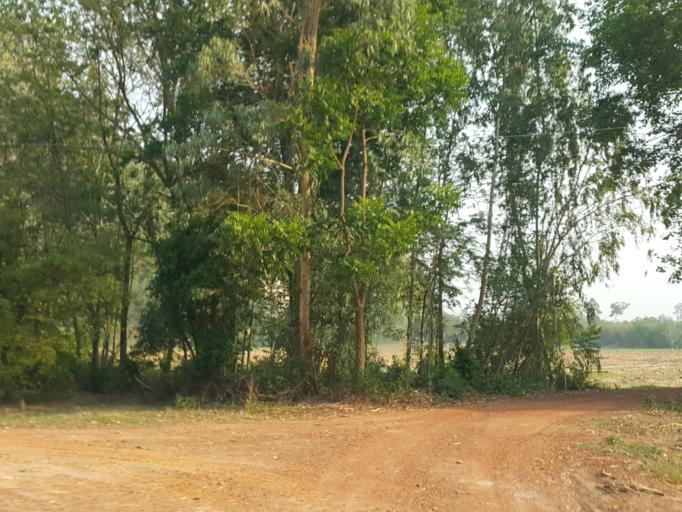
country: TH
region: Uthai Thani
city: Huai Khot
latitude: 15.3222
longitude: 99.6771
